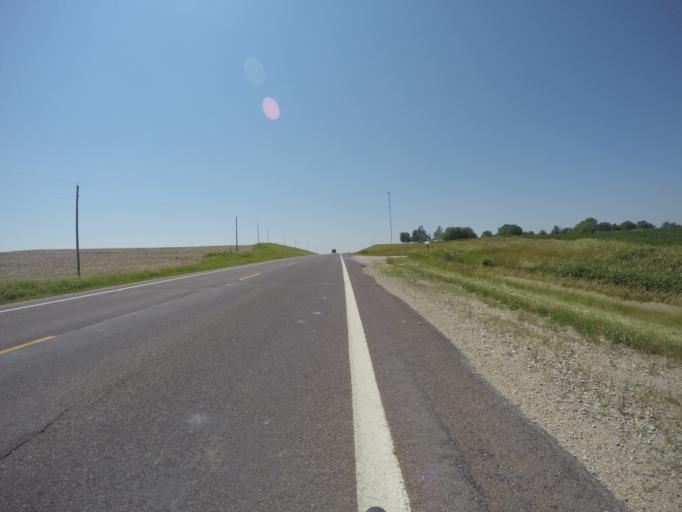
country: US
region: Kansas
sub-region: Doniphan County
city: Highland
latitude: 39.8513
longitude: -95.2652
